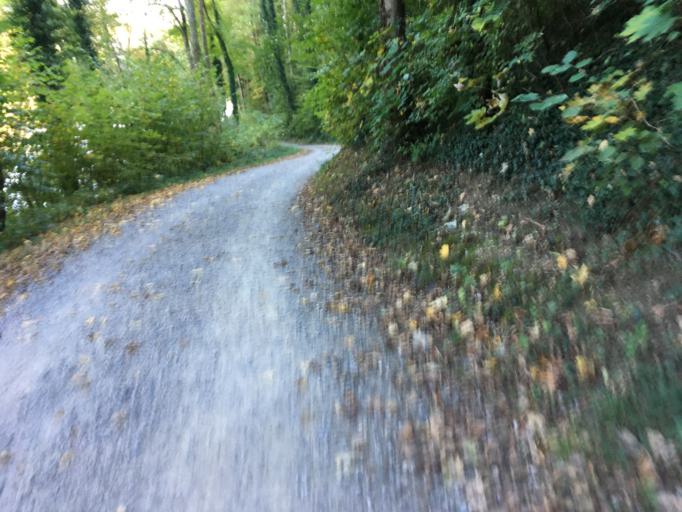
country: CH
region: Zurich
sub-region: Bezirk Buelach
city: Buelach / Soligaenter
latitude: 47.5559
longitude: 8.5498
